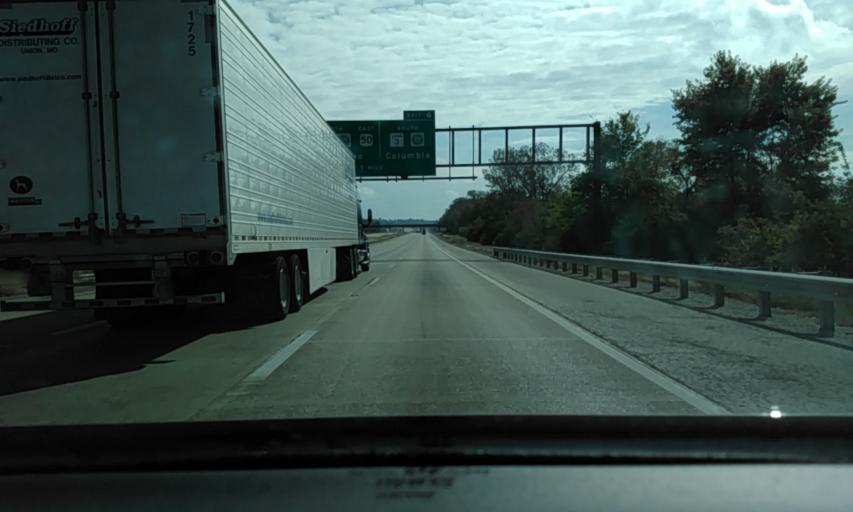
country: US
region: Missouri
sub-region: Saint Louis County
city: Oakville
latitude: 38.4802
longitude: -90.2545
